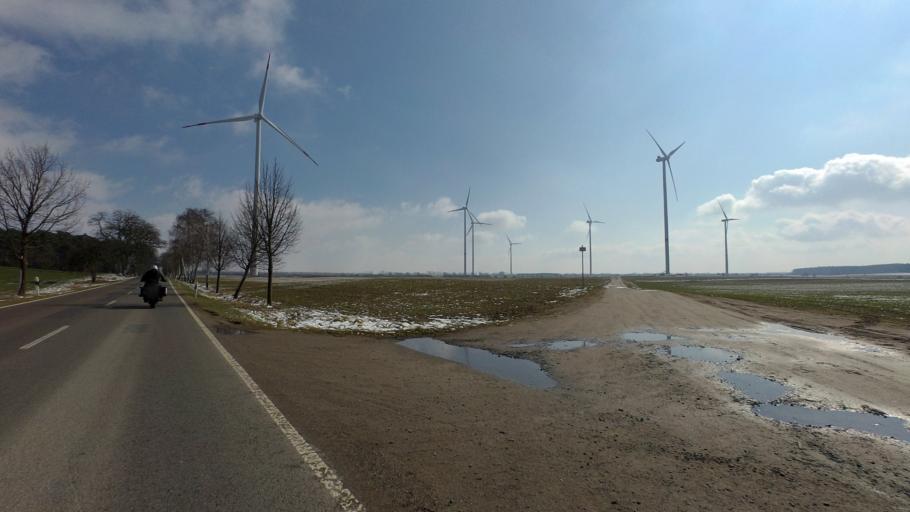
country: DE
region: Brandenburg
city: Rudnitz
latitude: 52.7013
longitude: 13.6904
